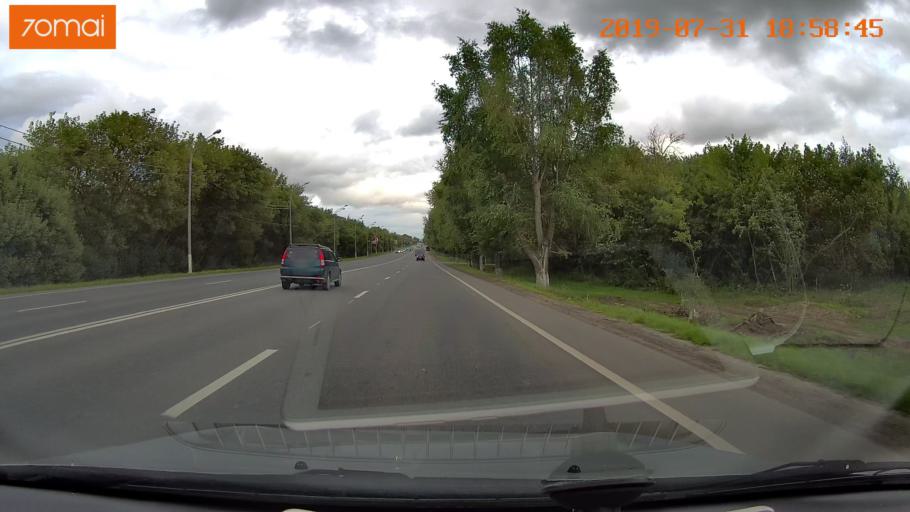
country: RU
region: Moskovskaya
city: Raduzhnyy
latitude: 55.1444
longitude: 38.7081
